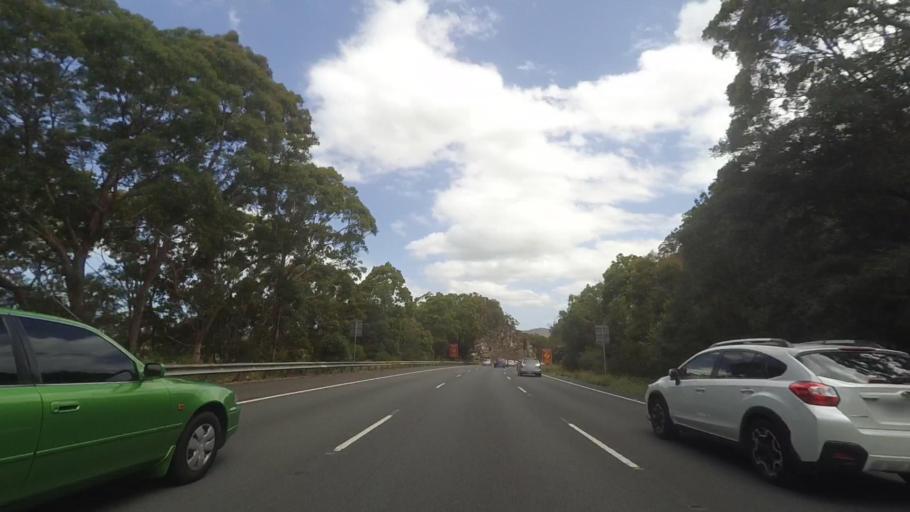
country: AU
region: New South Wales
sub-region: Hornsby Shire
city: Berowra Heights
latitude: -33.5179
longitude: 151.1965
